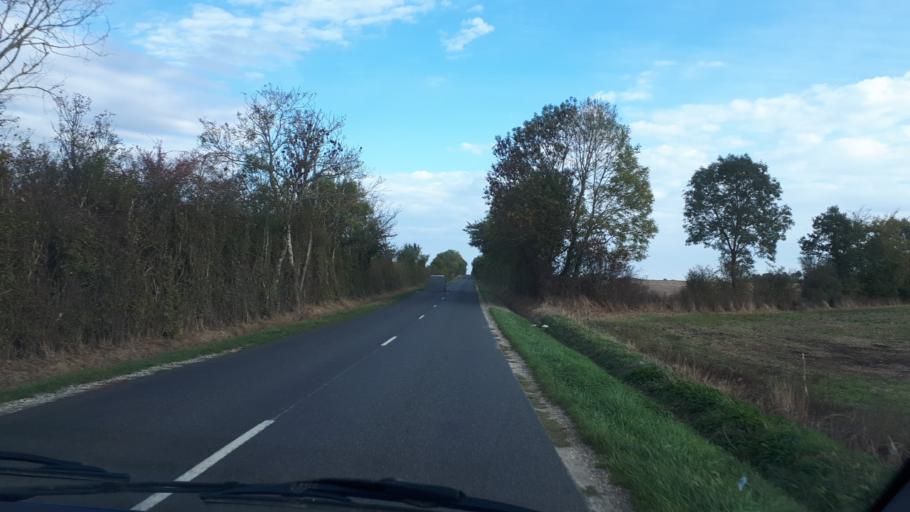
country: FR
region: Centre
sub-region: Departement du Loir-et-Cher
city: Mondoubleau
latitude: 47.9206
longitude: 0.9321
